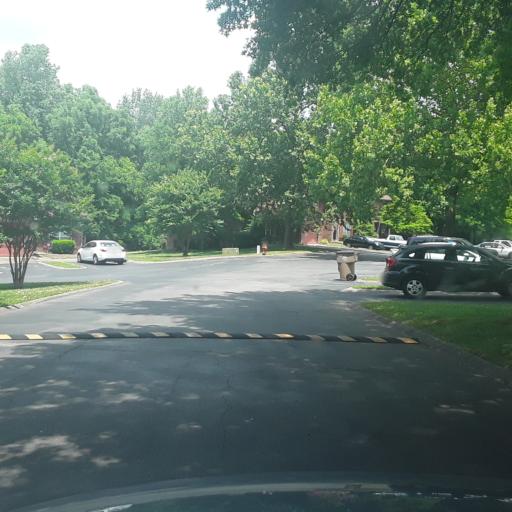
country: US
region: Tennessee
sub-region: Williamson County
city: Brentwood Estates
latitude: 36.0604
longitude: -86.7049
